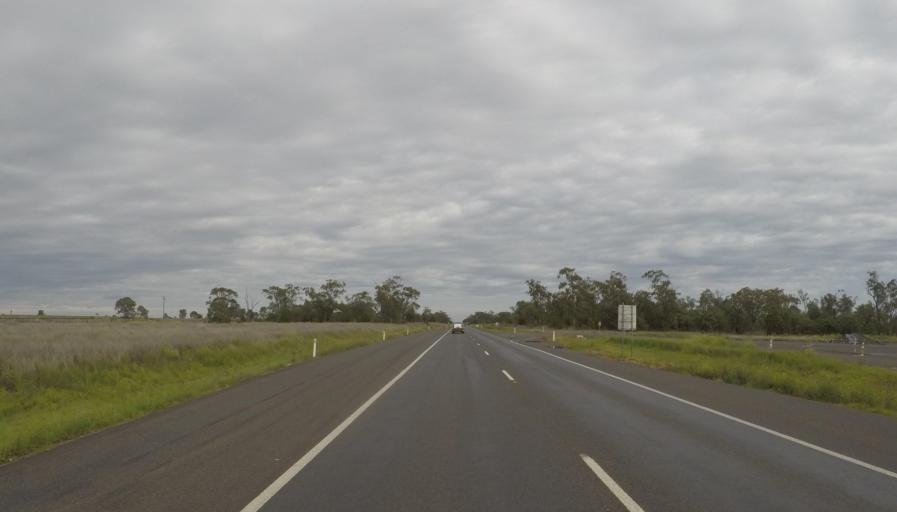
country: AU
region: Queensland
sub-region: Maranoa
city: Roma
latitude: -26.5869
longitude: 149.0387
